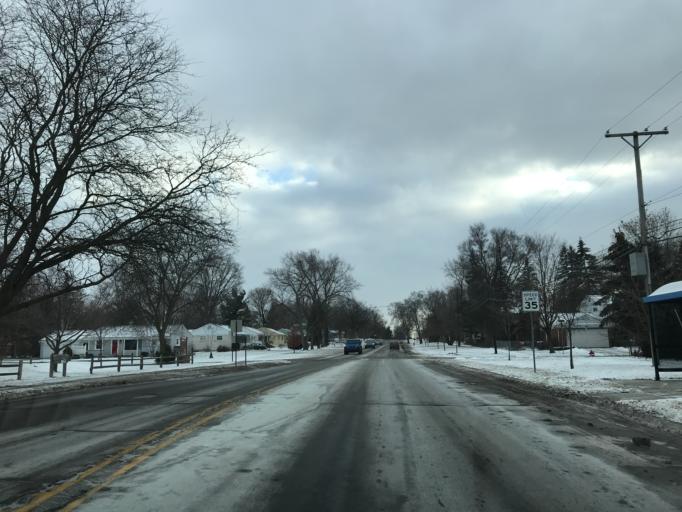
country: US
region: Michigan
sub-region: Washtenaw County
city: Ann Arbor
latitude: 42.2435
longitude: -83.7199
